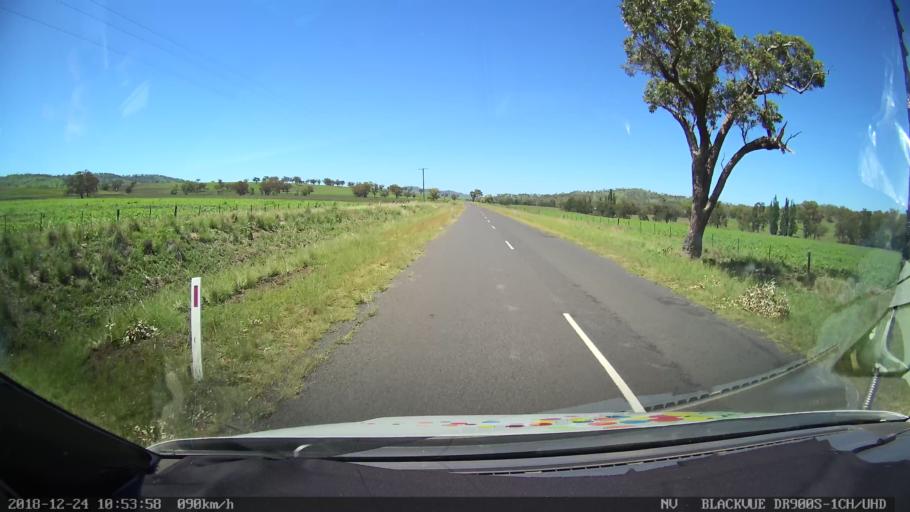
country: AU
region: New South Wales
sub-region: Upper Hunter Shire
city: Merriwa
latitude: -31.9978
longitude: 150.4188
